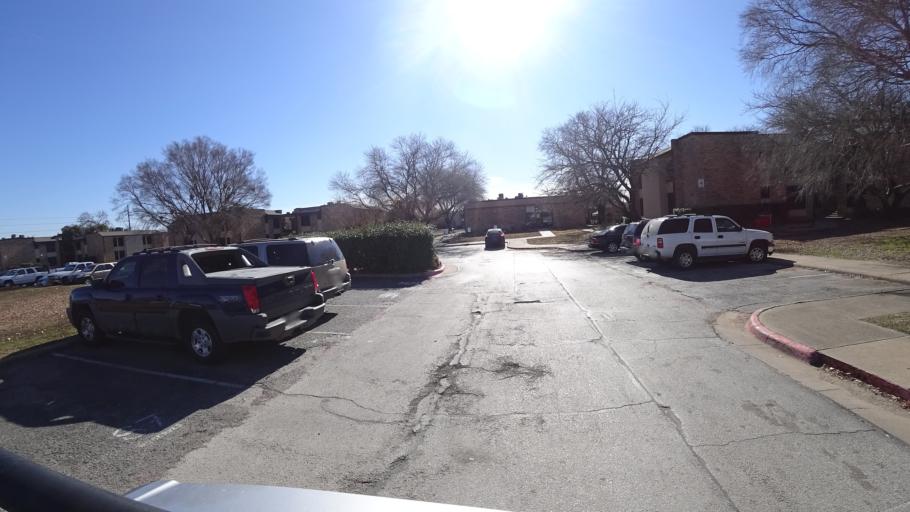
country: US
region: Texas
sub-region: Denton County
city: Lewisville
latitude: 33.0337
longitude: -97.0121
